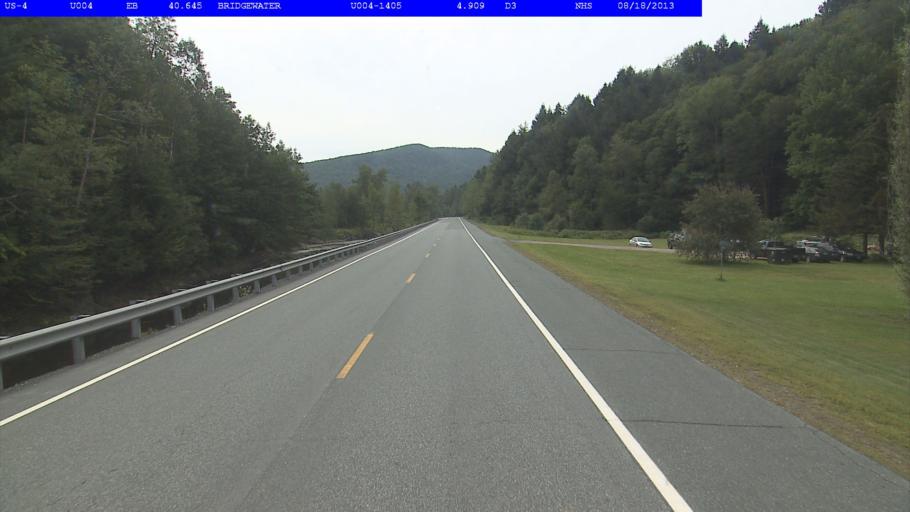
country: US
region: Vermont
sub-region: Windsor County
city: Woodstock
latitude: 43.5951
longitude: -72.6670
